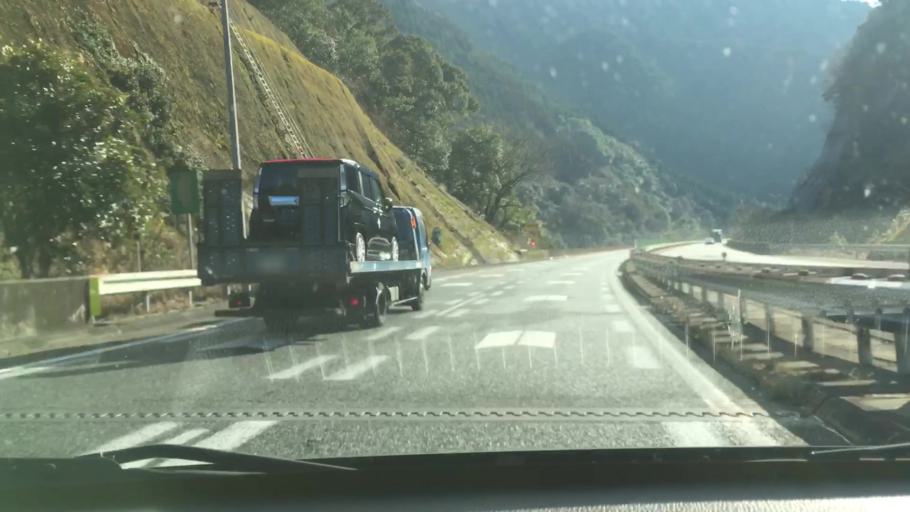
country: JP
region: Kumamoto
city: Hitoyoshi
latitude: 32.3235
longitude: 130.7582
